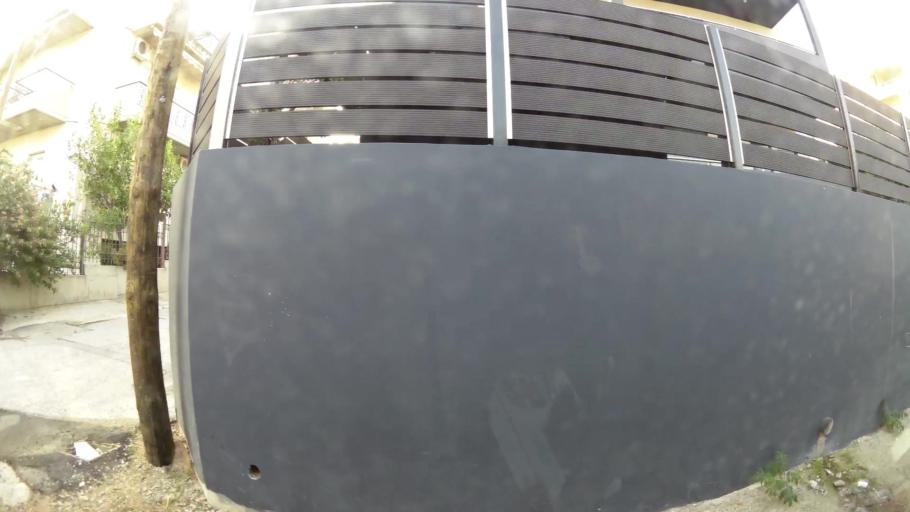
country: GR
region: Attica
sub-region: Nomarchia Dytikis Attikis
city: Zefyri
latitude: 38.0571
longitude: 23.7181
